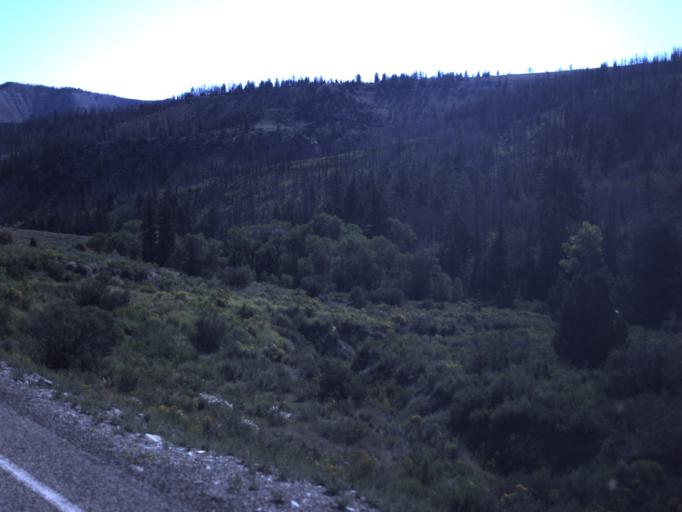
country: US
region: Utah
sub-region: Carbon County
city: Helper
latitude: 39.9135
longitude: -110.6969
